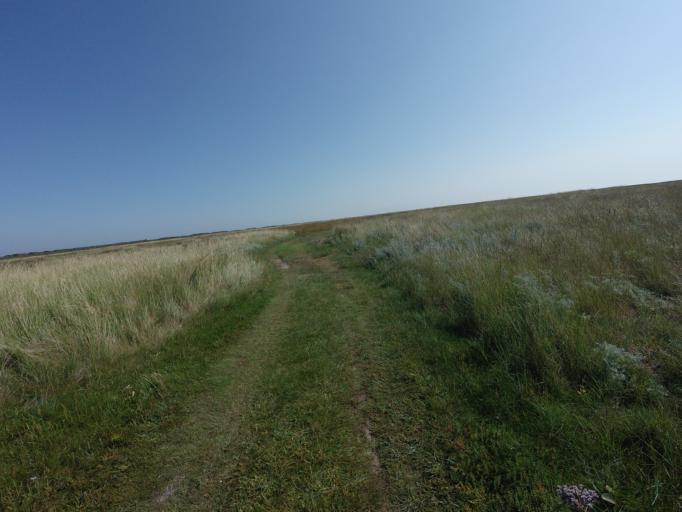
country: NL
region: Friesland
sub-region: Gemeente Schiermonnikoog
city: Schiermonnikoog
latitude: 53.4899
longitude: 6.2316
